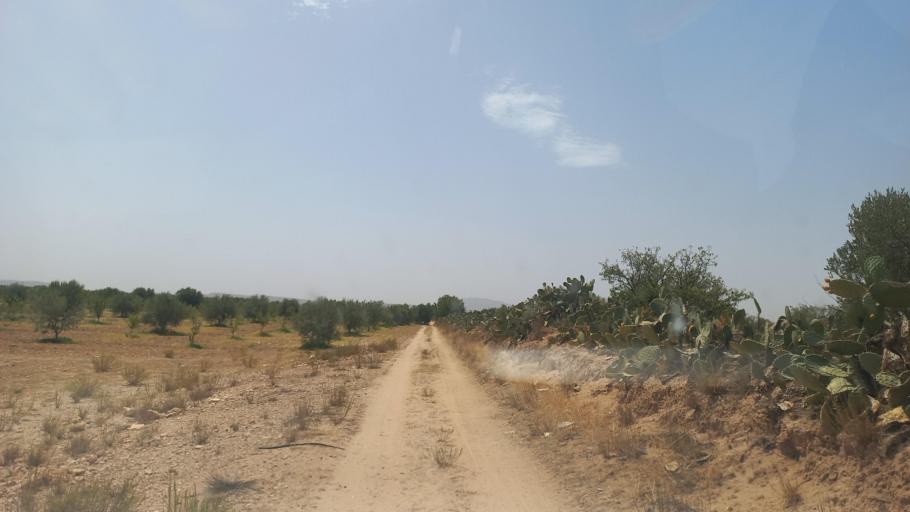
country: TN
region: Al Qasrayn
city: Kasserine
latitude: 35.2621
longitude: 9.0057
